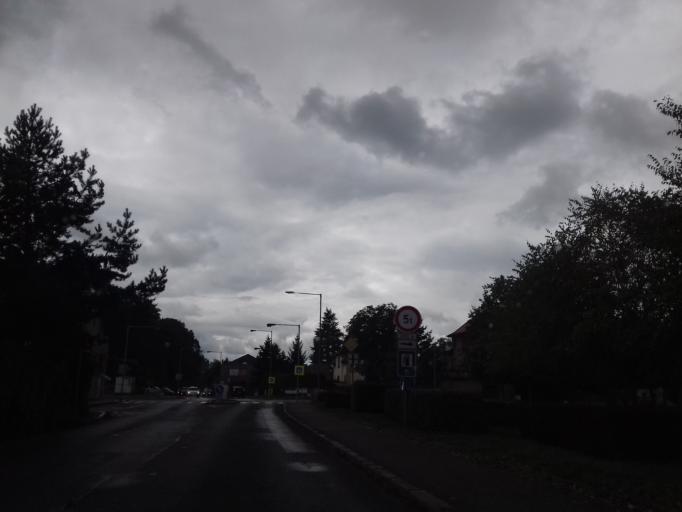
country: CZ
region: Central Bohemia
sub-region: Okres Praha-Zapad
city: Dobrichovice
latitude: 49.9281
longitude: 14.2718
